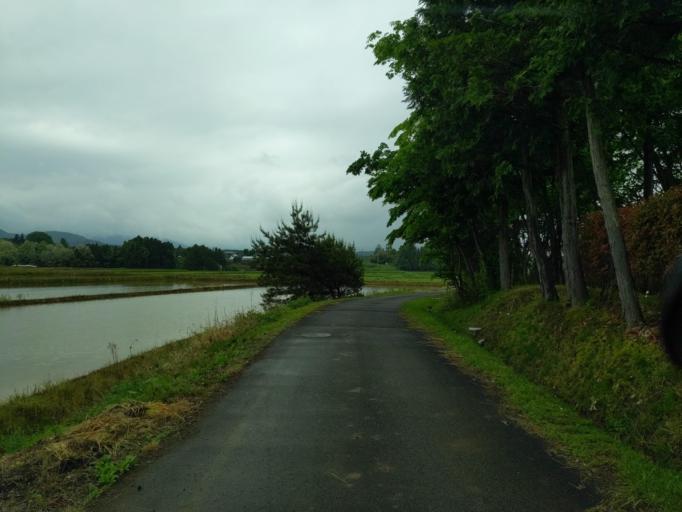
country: JP
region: Fukushima
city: Koriyama
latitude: 37.3513
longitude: 140.2858
